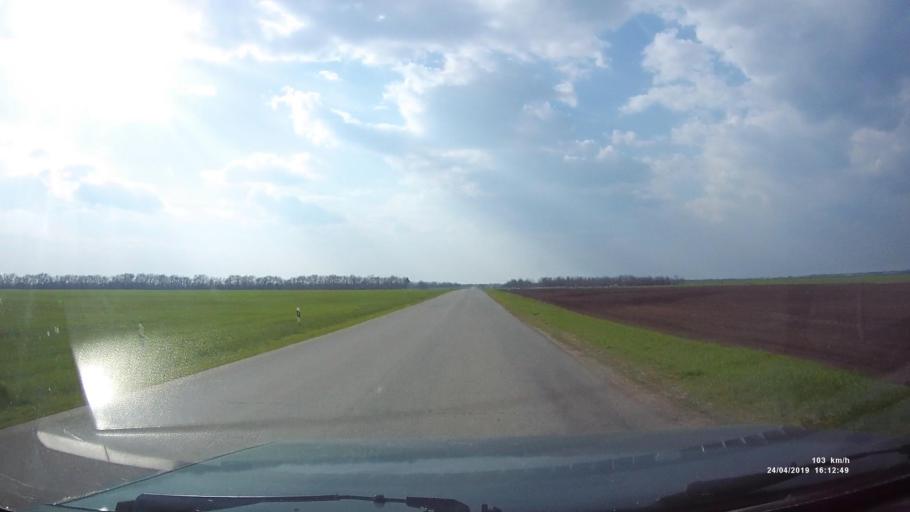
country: RU
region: Rostov
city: Sovetskoye
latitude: 46.7360
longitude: 42.2299
